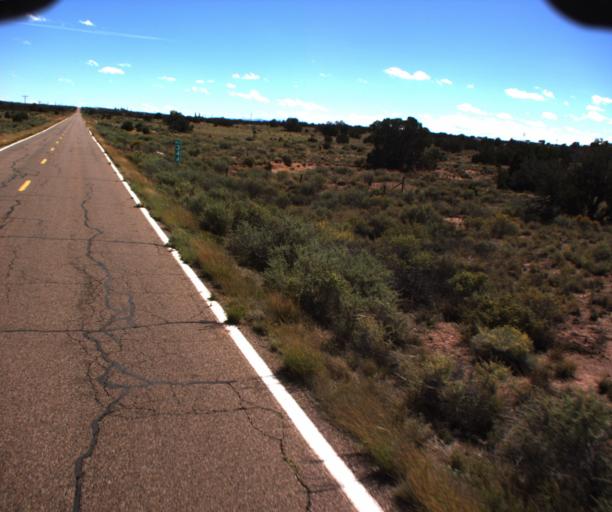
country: US
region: Arizona
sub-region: Apache County
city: Saint Johns
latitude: 34.6084
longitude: -109.6567
